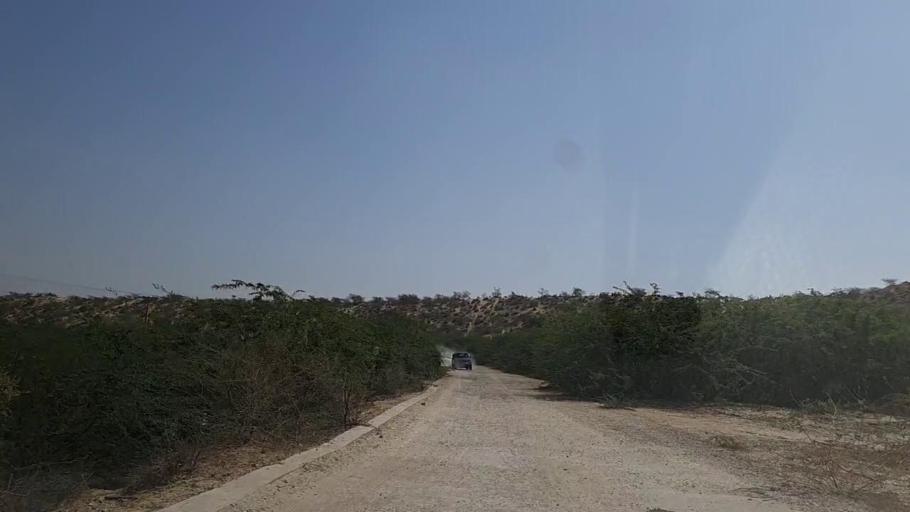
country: PK
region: Sindh
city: Diplo
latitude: 24.5143
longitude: 69.3668
